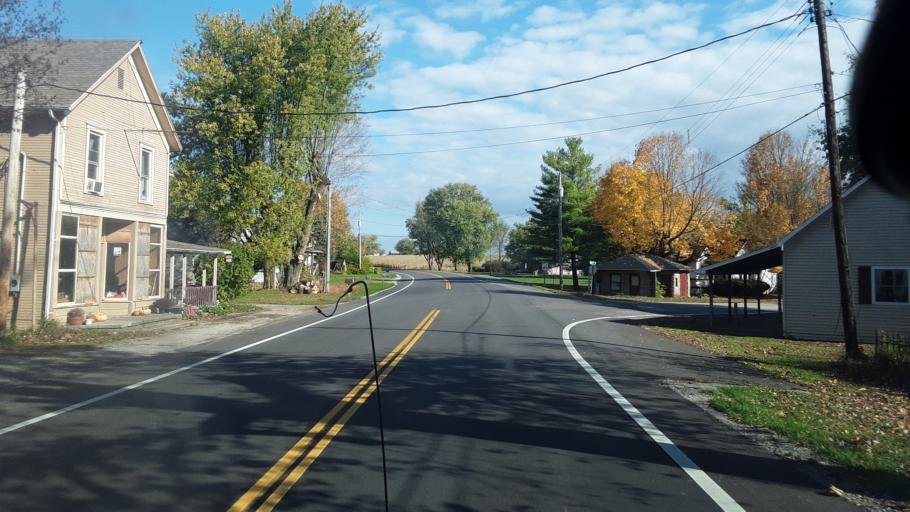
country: US
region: Ohio
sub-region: Highland County
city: Leesburg
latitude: 39.2847
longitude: -83.5919
